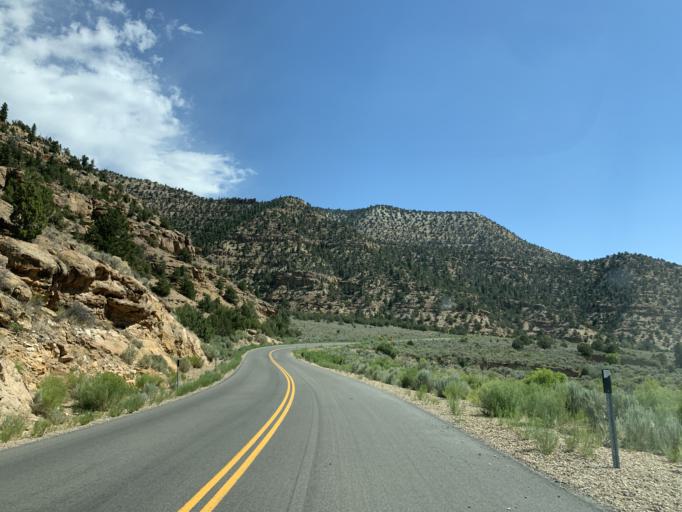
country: US
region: Utah
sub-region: Carbon County
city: East Carbon City
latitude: 39.7850
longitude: -110.4187
